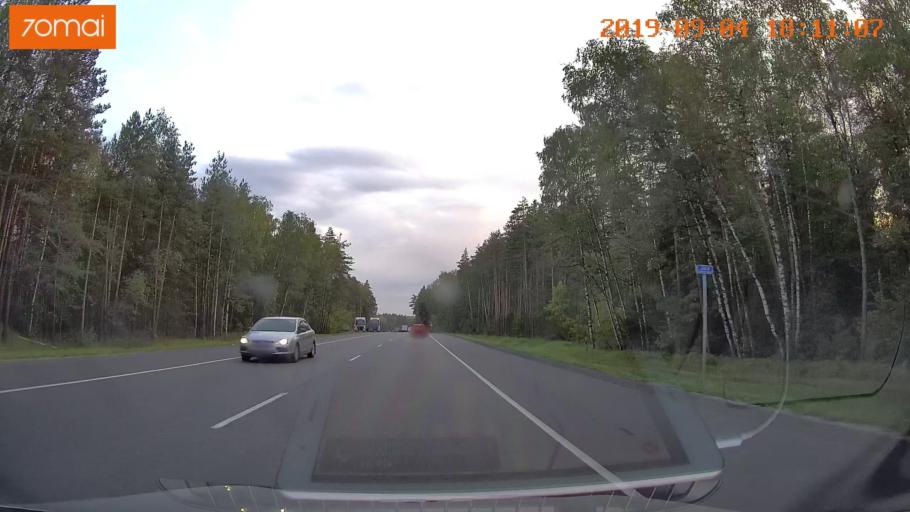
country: RU
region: Moskovskaya
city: Lopatinskiy
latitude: 55.3811
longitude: 38.7578
